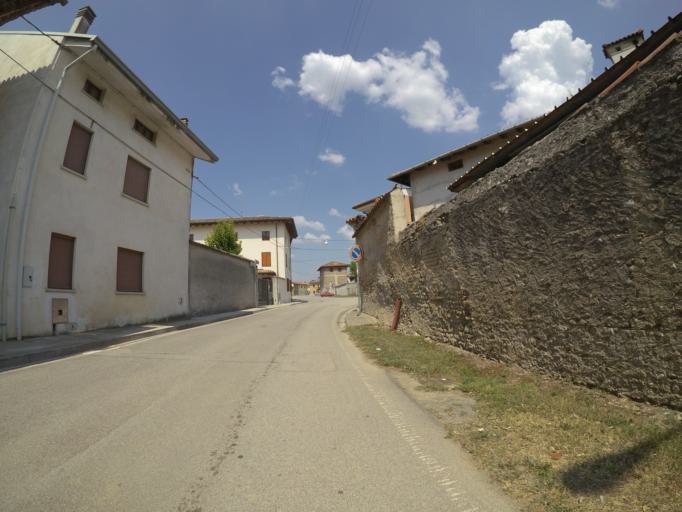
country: IT
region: Friuli Venezia Giulia
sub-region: Provincia di Udine
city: Bertiolo
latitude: 45.9356
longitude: 13.0712
